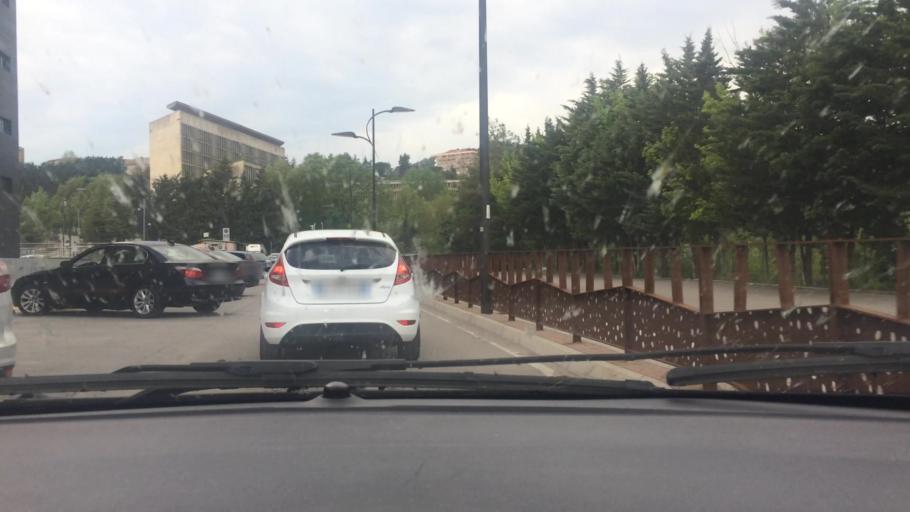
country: IT
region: Basilicate
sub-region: Provincia di Potenza
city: Potenza
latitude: 40.6531
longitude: 15.8067
